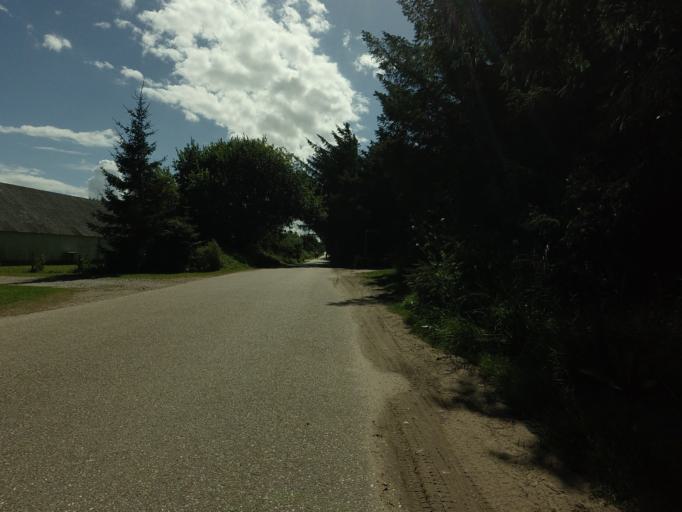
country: DK
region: North Denmark
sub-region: Jammerbugt Kommune
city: Pandrup
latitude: 57.3223
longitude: 9.6663
